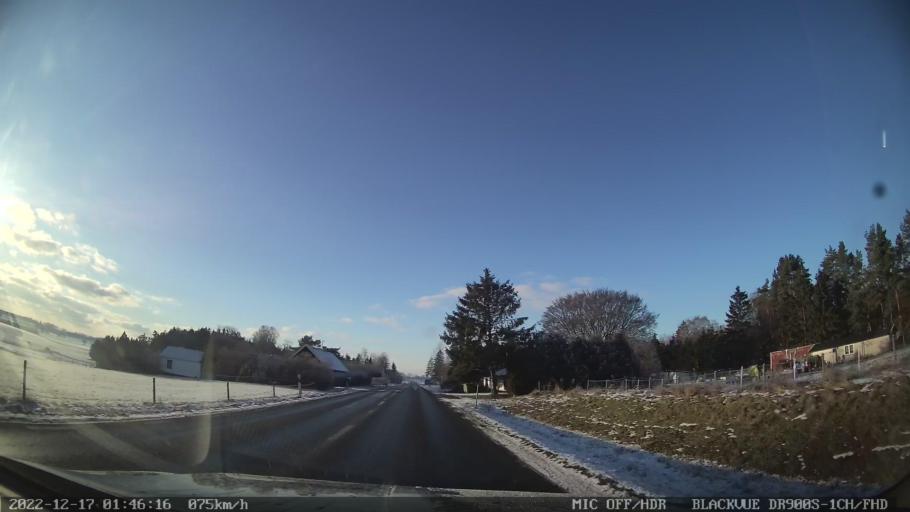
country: SE
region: Skane
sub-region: Tomelilla Kommun
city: Tomelilla
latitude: 55.5543
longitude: 14.0913
